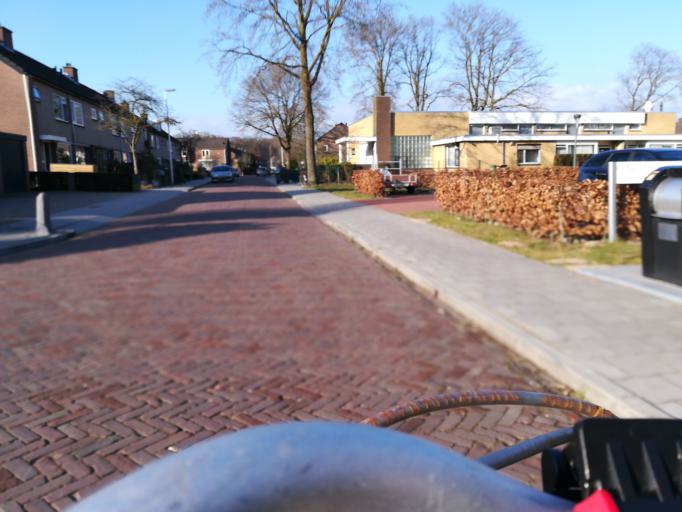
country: NL
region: Gelderland
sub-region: Gemeente Epe
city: Epe
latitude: 52.3419
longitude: 5.9764
